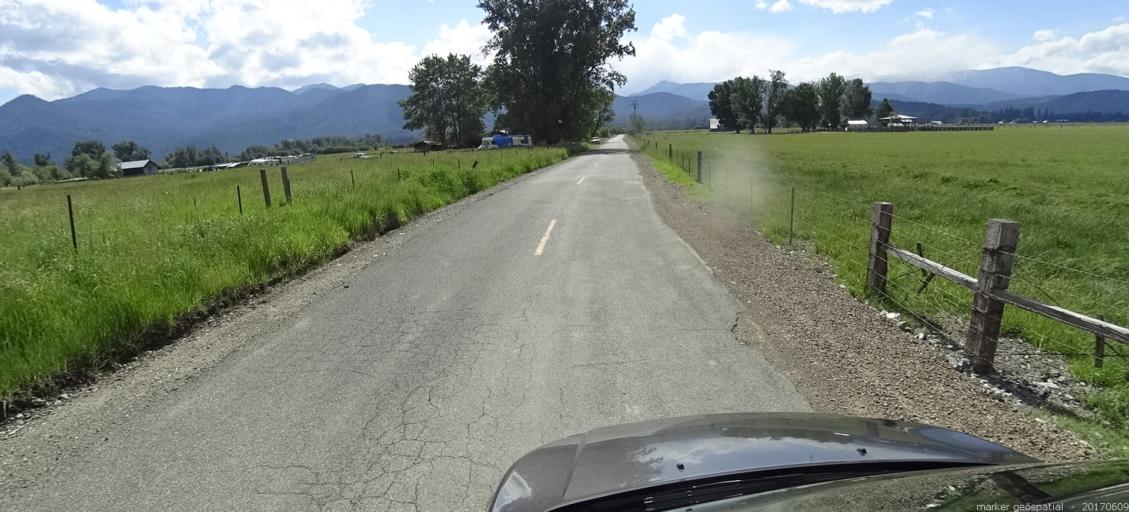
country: US
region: California
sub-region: Siskiyou County
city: Yreka
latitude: 41.5131
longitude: -122.8808
